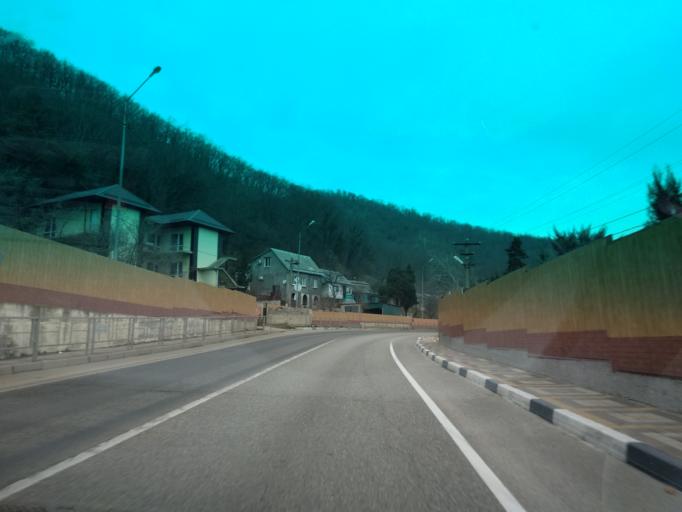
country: RU
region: Krasnodarskiy
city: Ol'ginka
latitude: 44.2023
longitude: 38.8867
